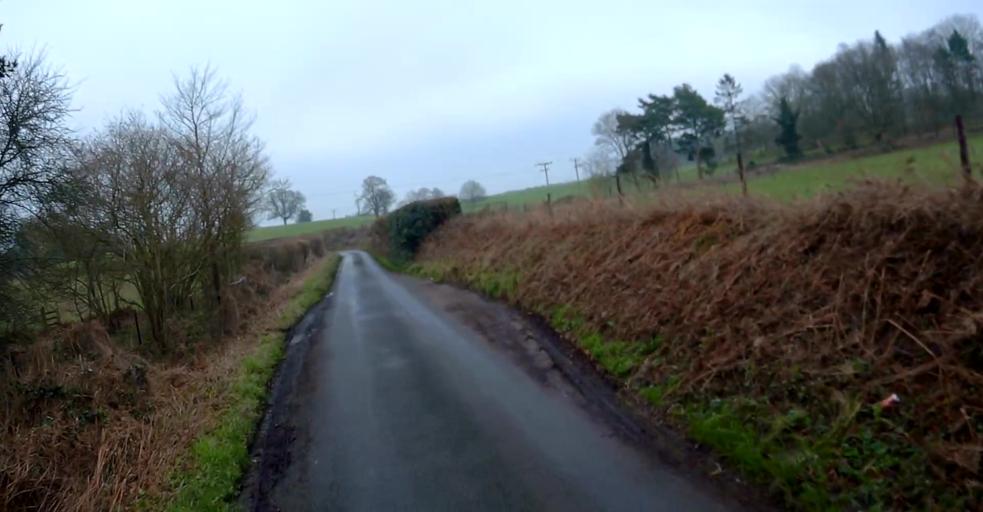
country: GB
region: England
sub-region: Hampshire
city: Eversley
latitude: 51.3367
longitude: -0.9244
